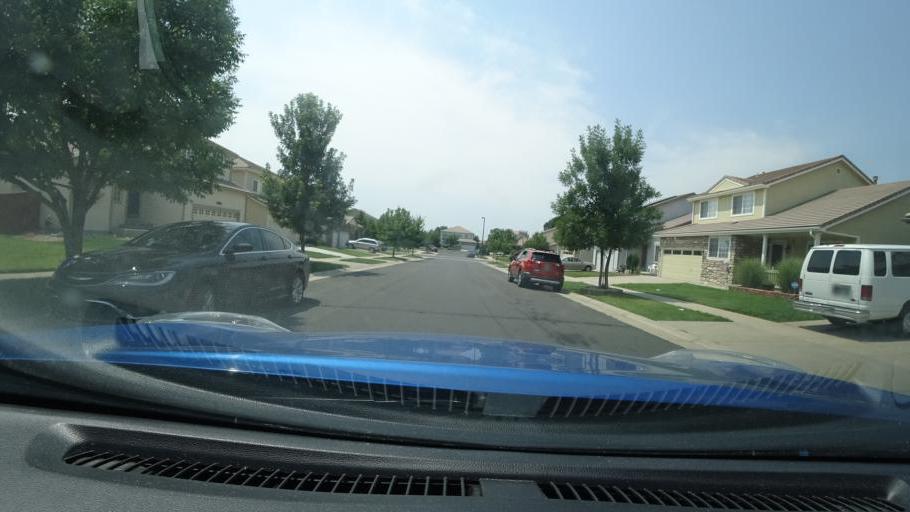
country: US
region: Colorado
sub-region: Adams County
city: Aurora
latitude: 39.7714
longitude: -104.7512
